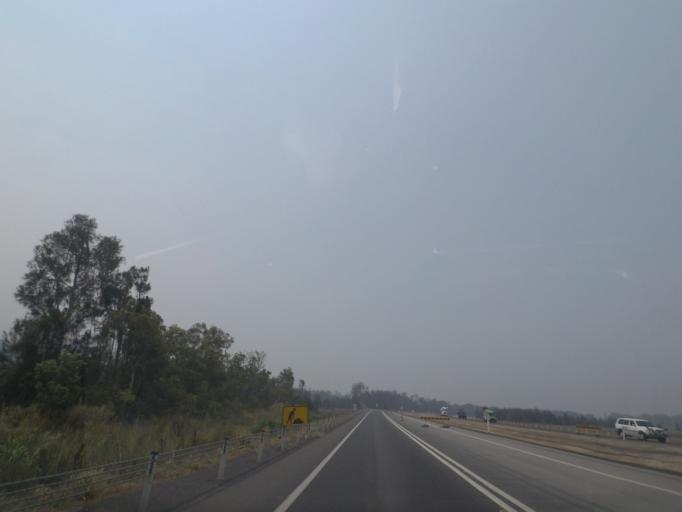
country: AU
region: New South Wales
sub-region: Ballina
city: Ballina
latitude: -28.8717
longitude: 153.4906
